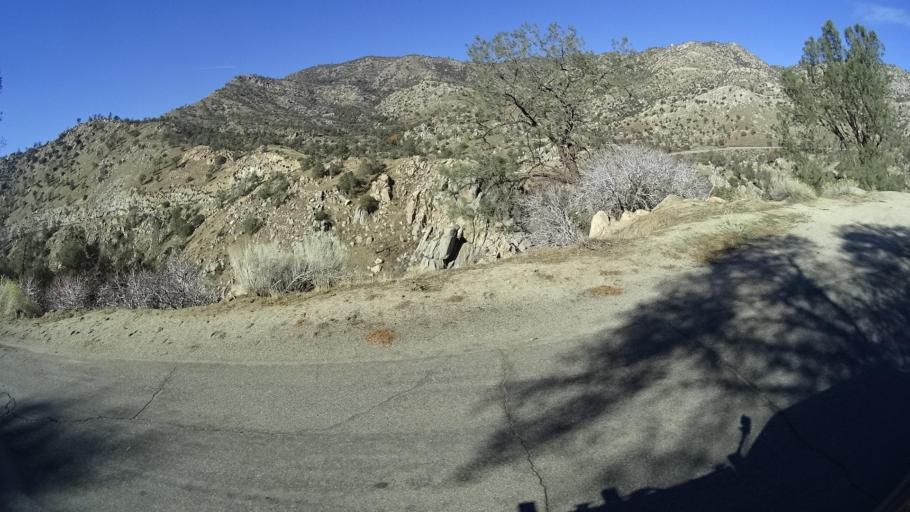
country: US
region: California
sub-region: Kern County
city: Bodfish
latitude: 35.5736
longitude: -118.5587
